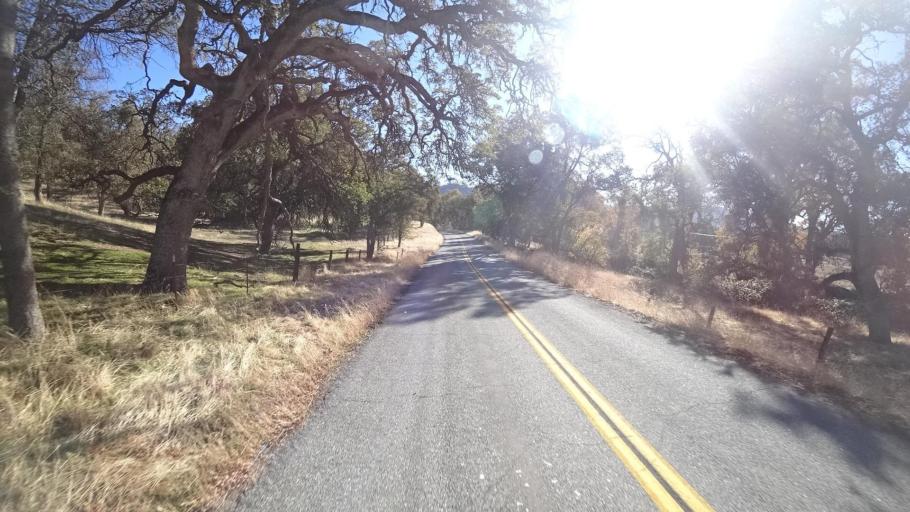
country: US
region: California
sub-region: Kern County
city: Alta Sierra
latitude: 35.7948
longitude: -118.7091
